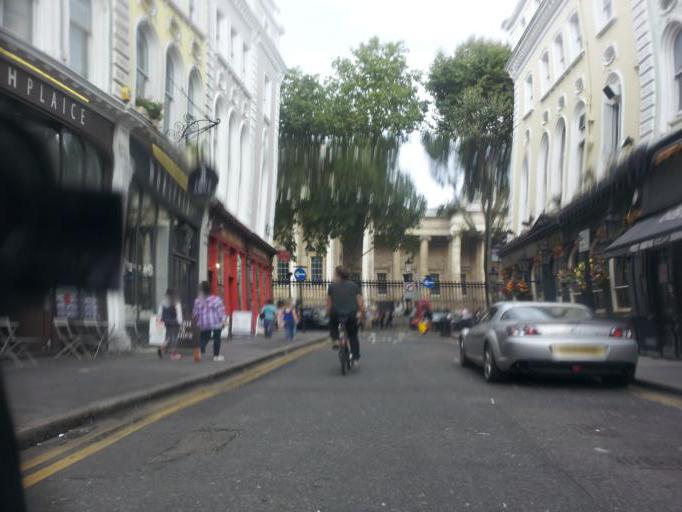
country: GB
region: England
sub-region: Greater London
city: London
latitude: 51.5179
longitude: -0.1257
